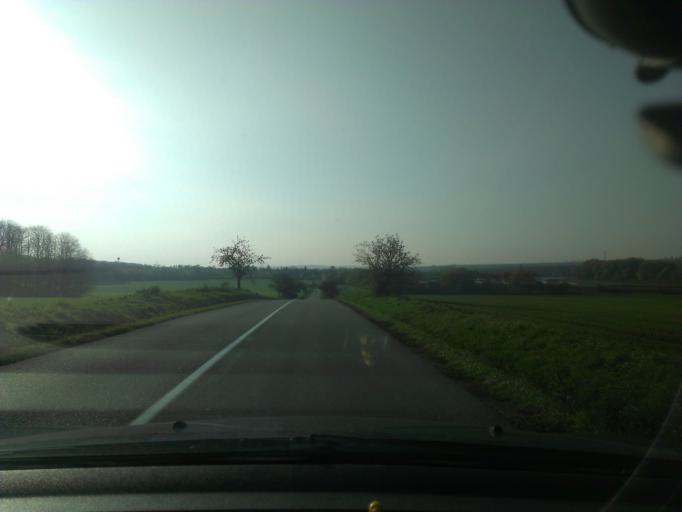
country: SK
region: Nitriansky
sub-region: Okres Nitra
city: Nitra
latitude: 48.4470
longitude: 17.9857
